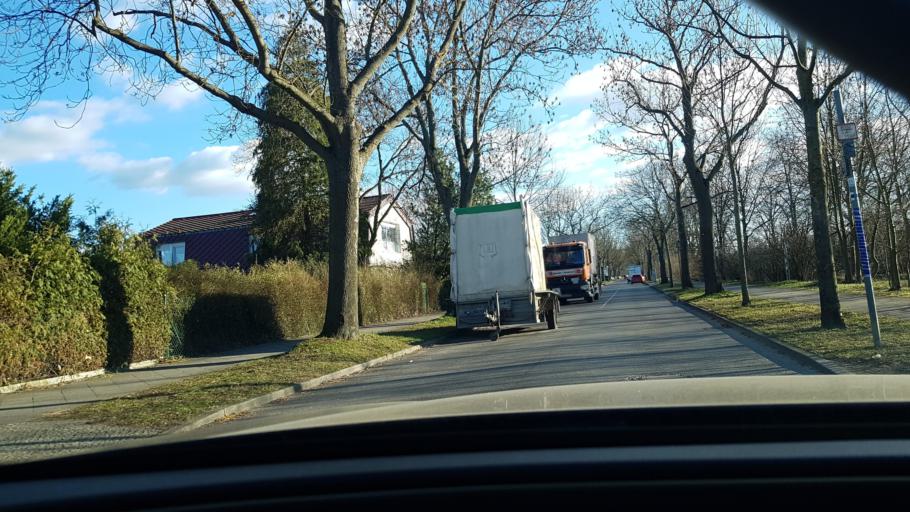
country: DE
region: Berlin
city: Rudow
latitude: 52.4045
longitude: 13.5002
